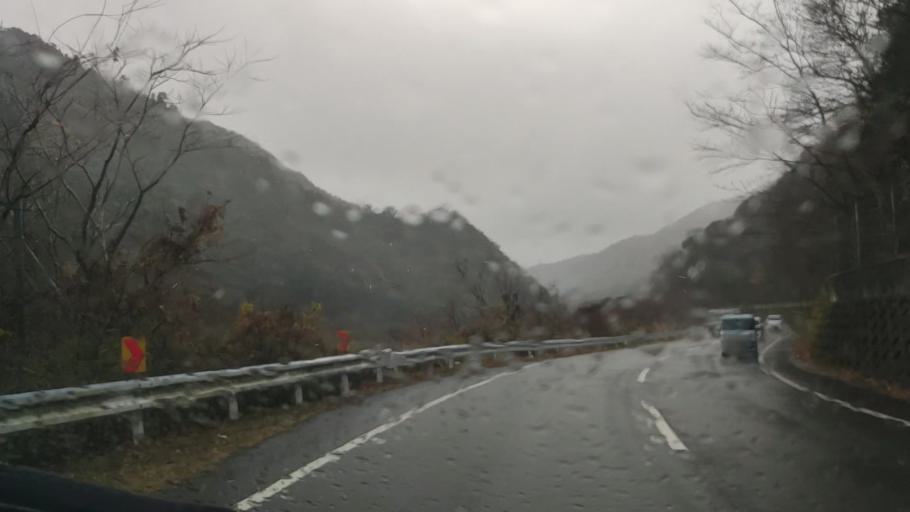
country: JP
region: Tokushima
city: Kamojimacho-jogejima
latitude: 34.1463
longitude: 134.3549
